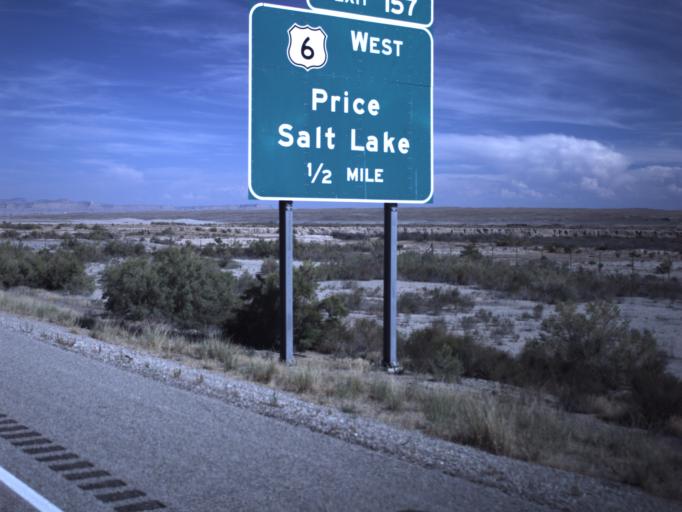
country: US
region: Utah
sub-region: Carbon County
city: East Carbon City
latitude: 38.9788
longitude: -110.2399
